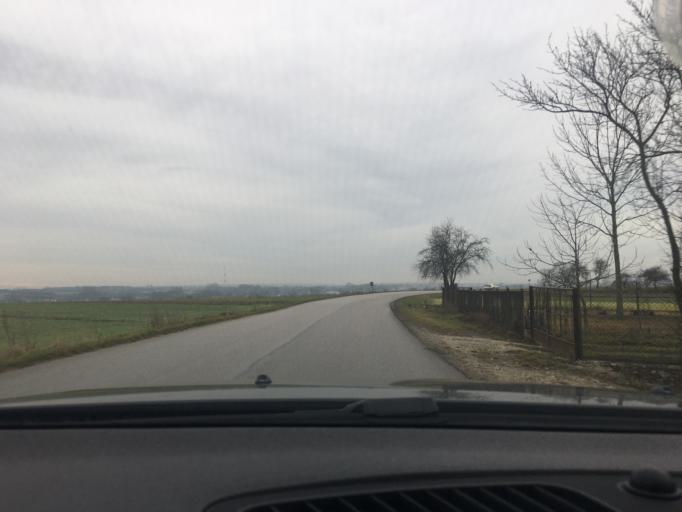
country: PL
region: Swietokrzyskie
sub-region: Powiat jedrzejowski
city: Jedrzejow
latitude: 50.6388
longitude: 20.3441
